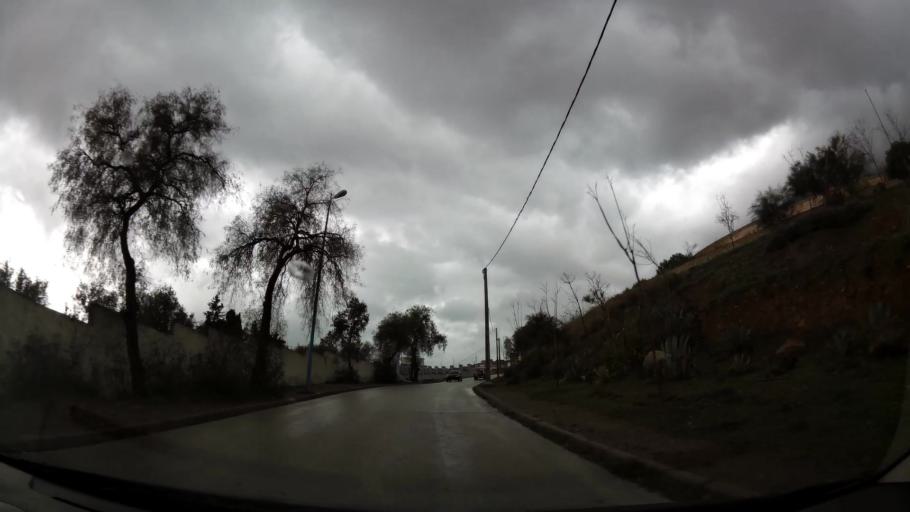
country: MA
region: Tanger-Tetouan
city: Chefchaouene
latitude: 35.1745
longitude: -5.2740
